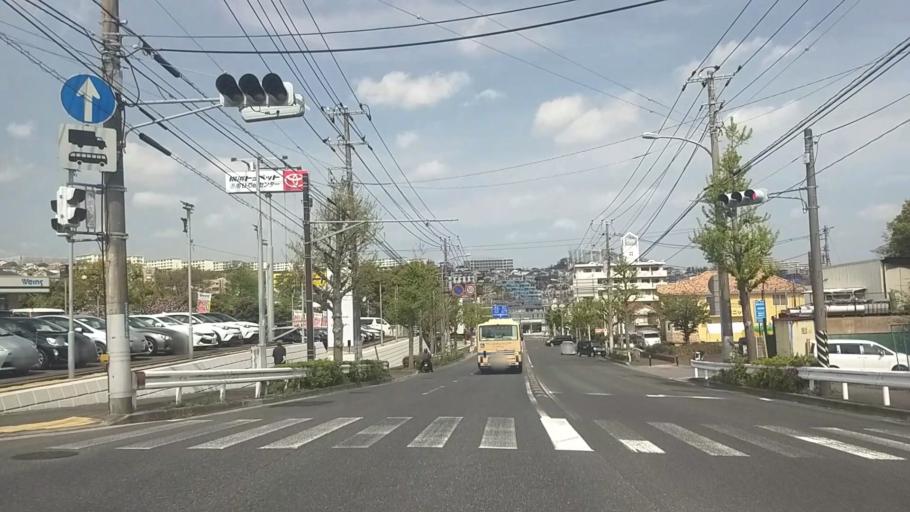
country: JP
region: Kanagawa
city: Yokohama
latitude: 35.3887
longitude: 139.5842
